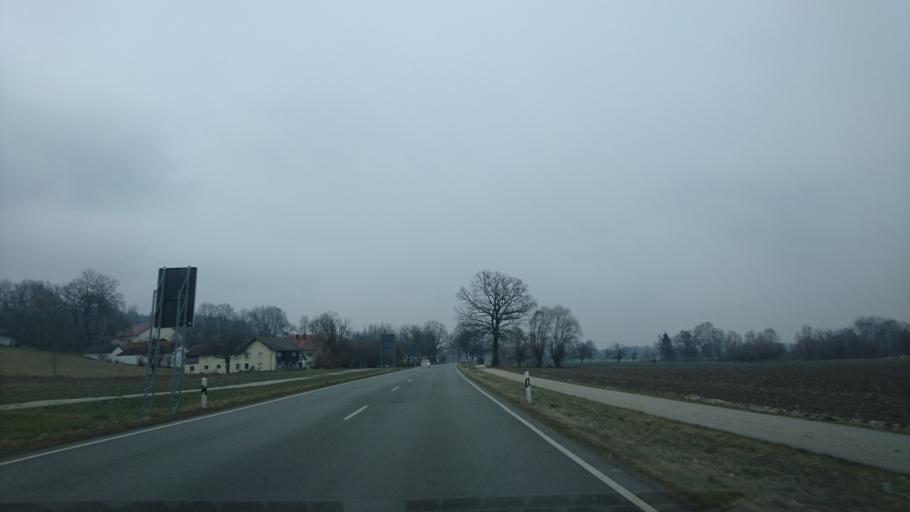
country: DE
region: Bavaria
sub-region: Lower Bavaria
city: Tettenweis
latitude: 48.4155
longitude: 13.2309
